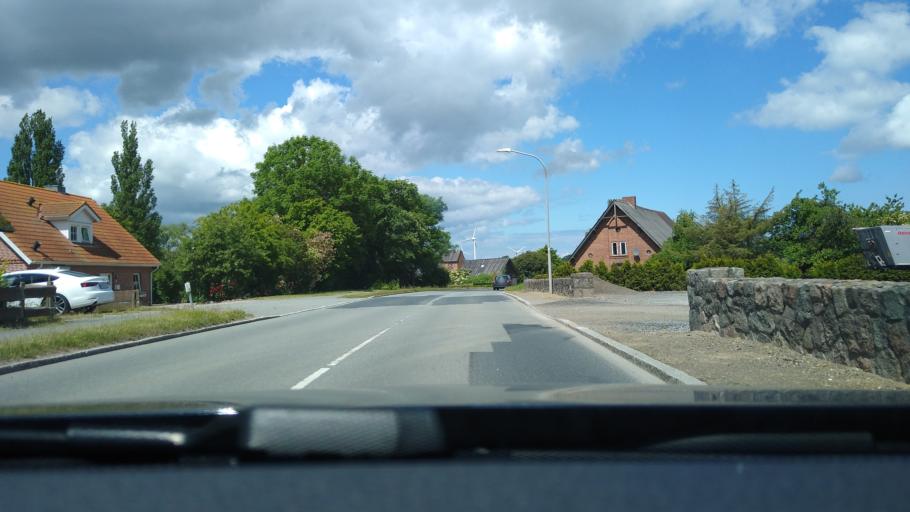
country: DE
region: Schleswig-Holstein
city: Kabelhorst
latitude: 54.2126
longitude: 10.9271
